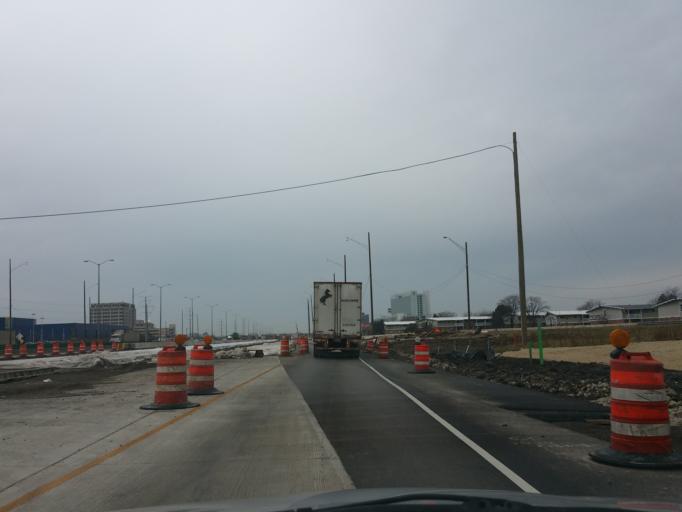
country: US
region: Illinois
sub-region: Cook County
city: Rolling Meadows
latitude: 42.0581
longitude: -88.0303
